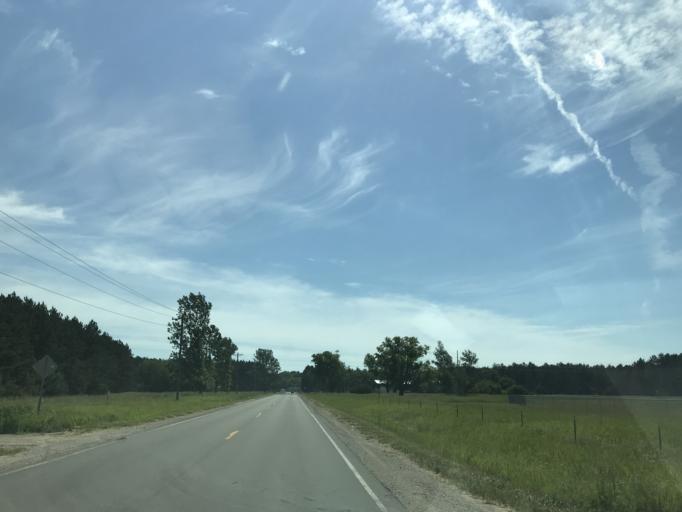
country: US
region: Michigan
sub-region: Grand Traverse County
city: Traverse City
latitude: 44.6542
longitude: -85.7030
